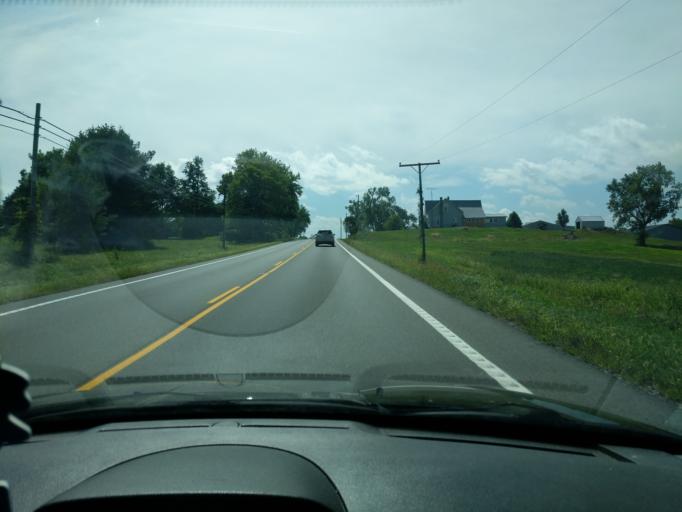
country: US
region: Ohio
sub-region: Logan County
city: Bellefontaine
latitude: 40.3118
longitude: -83.7600
